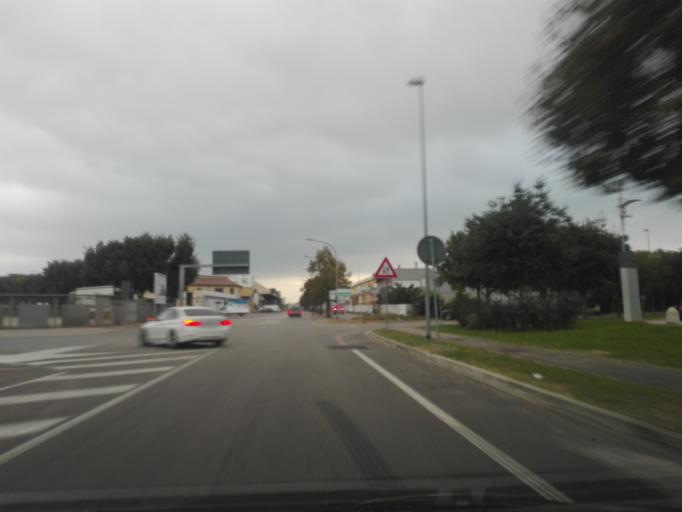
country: IT
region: Veneto
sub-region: Provincia di Verona
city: Verona
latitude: 45.4141
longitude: 10.9714
